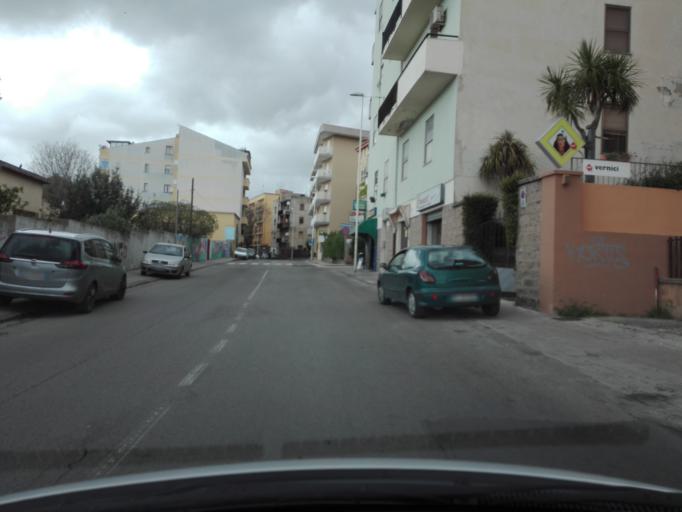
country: IT
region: Sardinia
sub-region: Provincia di Sassari
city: Sassari
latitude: 40.7329
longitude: 8.5694
